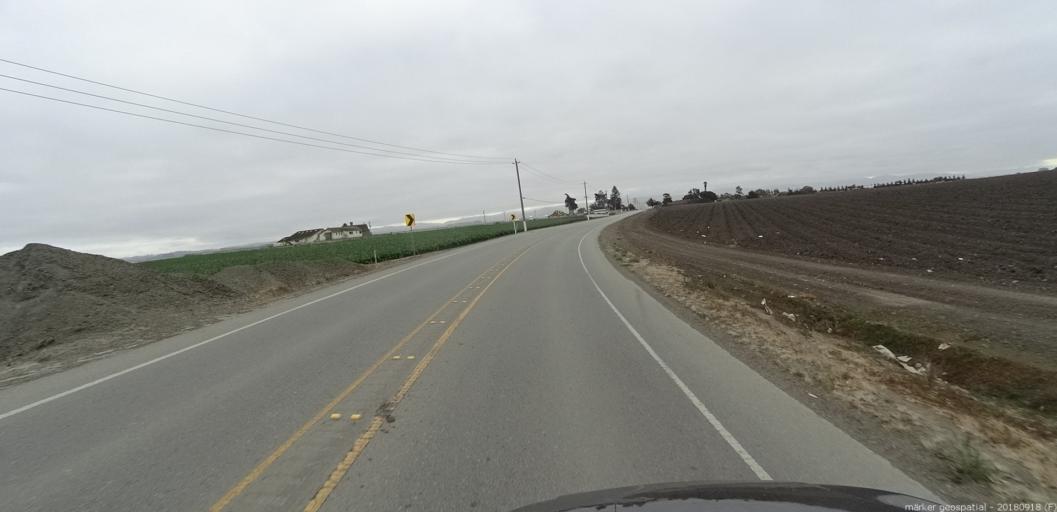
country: US
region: California
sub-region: Monterey County
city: Castroville
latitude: 36.7479
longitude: -121.7233
